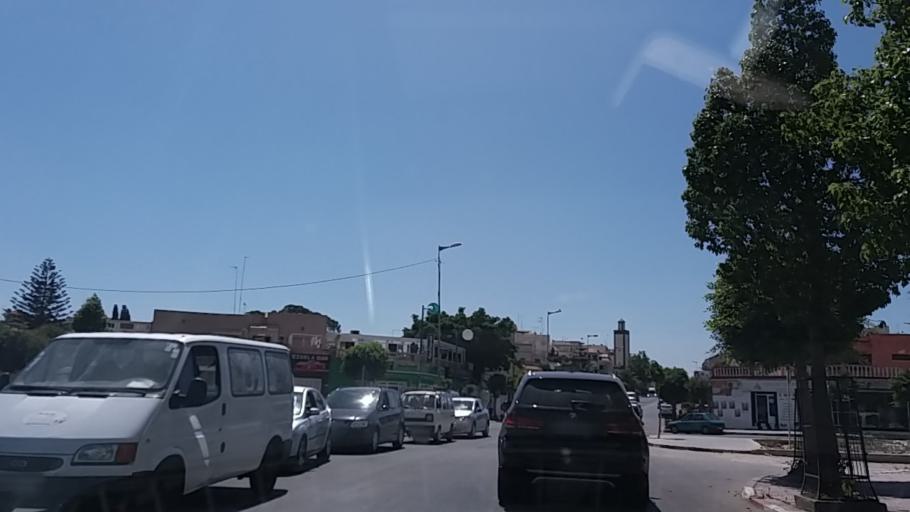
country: MA
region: Tanger-Tetouan
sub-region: Tanger-Assilah
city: Tangier
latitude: 35.7664
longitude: -5.8053
